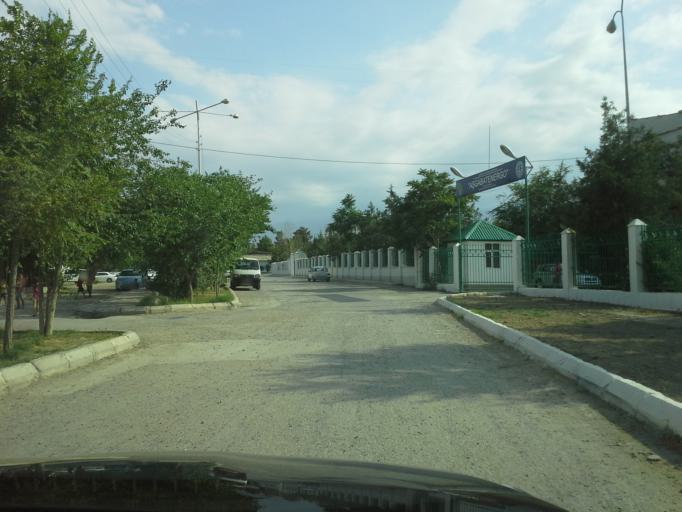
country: TM
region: Ahal
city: Ashgabat
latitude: 37.9577
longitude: 58.3425
